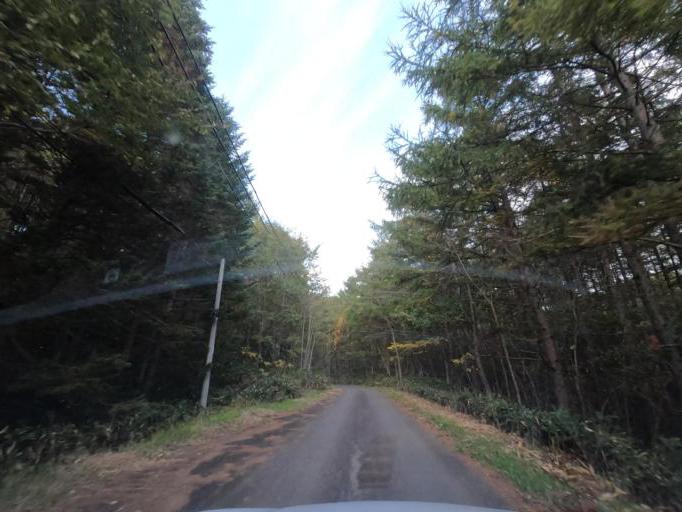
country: JP
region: Hokkaido
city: Obihiro
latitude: 42.5882
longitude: 143.3111
